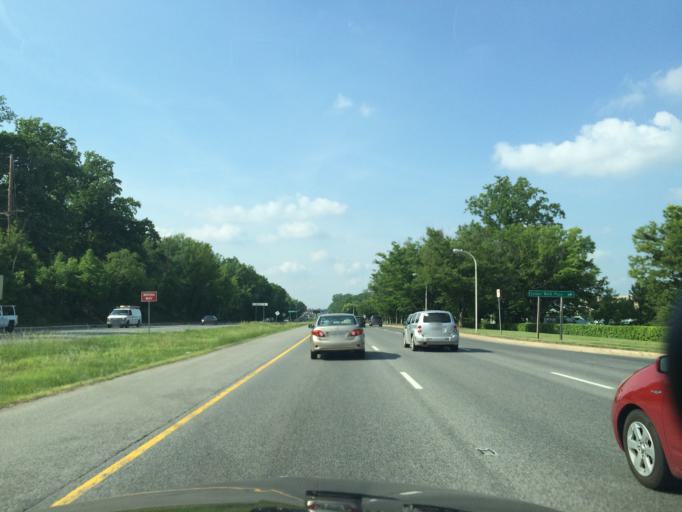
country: US
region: Maryland
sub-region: Montgomery County
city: Rossmoor
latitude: 39.1013
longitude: -77.0769
